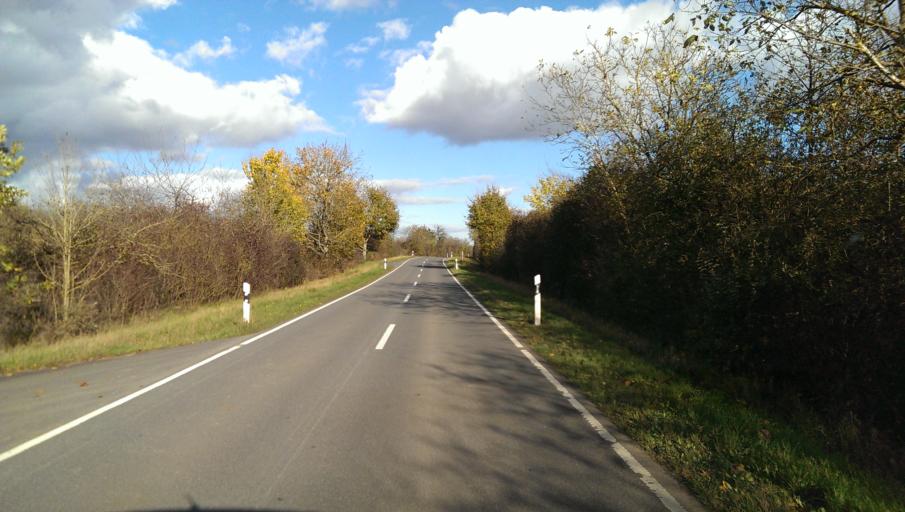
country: DE
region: Baden-Wuerttemberg
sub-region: Karlsruhe Region
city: Buchen
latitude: 49.4931
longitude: 9.3843
